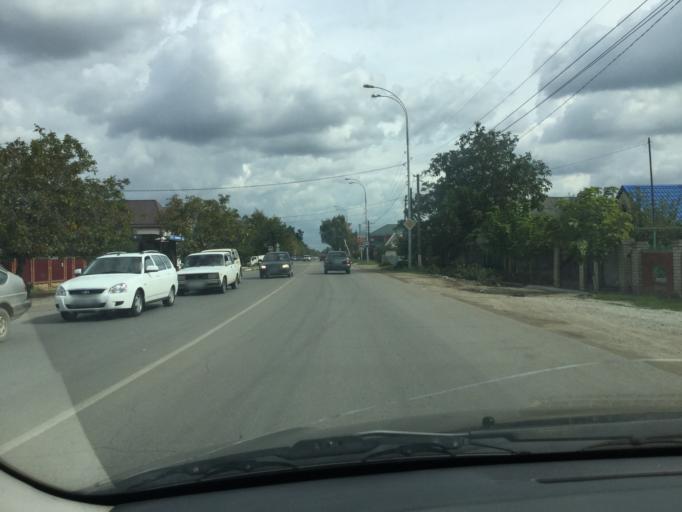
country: RU
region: Krasnodarskiy
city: Slavyansk-na-Kubani
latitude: 45.2495
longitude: 38.1005
